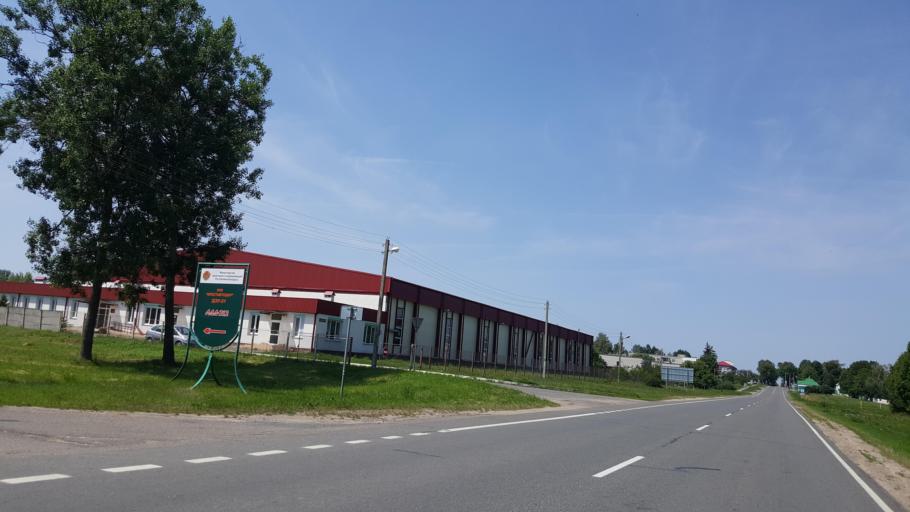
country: BY
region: Brest
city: Vysokaye
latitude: 52.3611
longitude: 23.4072
